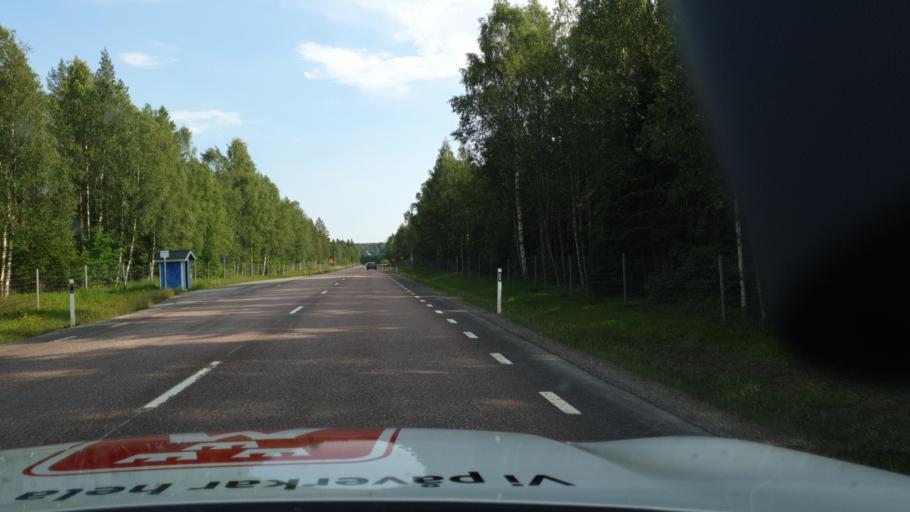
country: SE
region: Vaesterbotten
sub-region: Skelleftea Kommun
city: Burea
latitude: 64.4105
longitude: 21.2952
